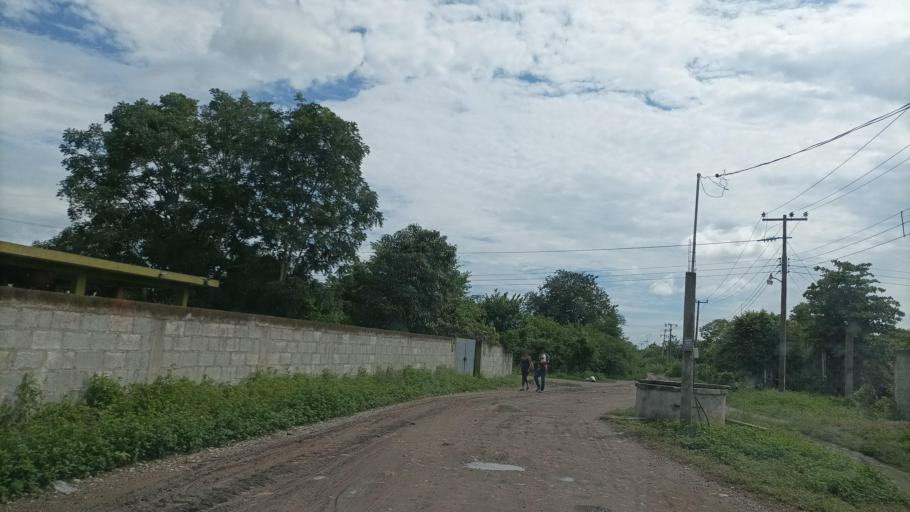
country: MX
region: Veracruz
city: Panuco
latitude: 21.9448
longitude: -98.1369
